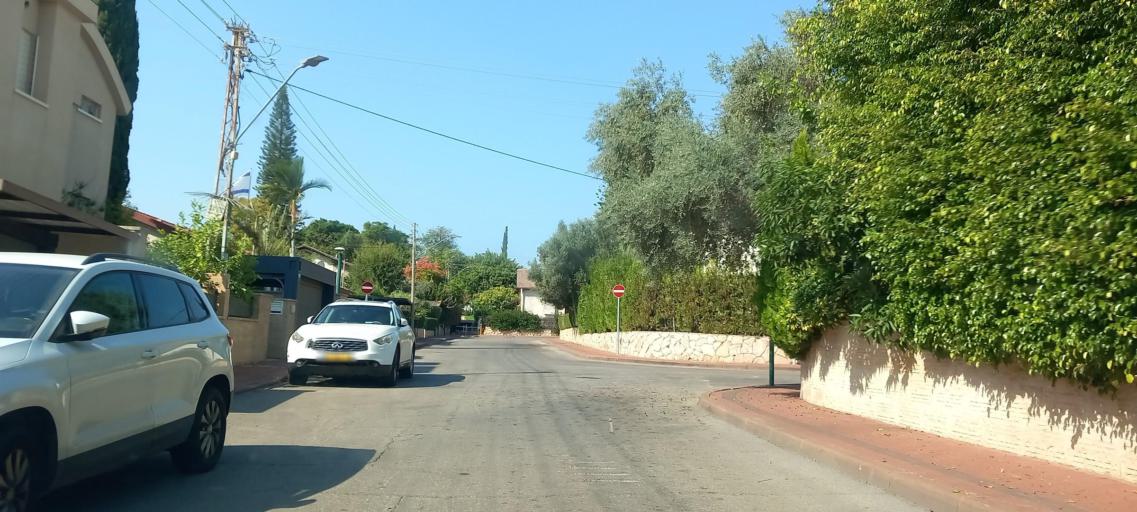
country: IL
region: Tel Aviv
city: Or Yehuda
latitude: 32.0465
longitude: 34.8368
